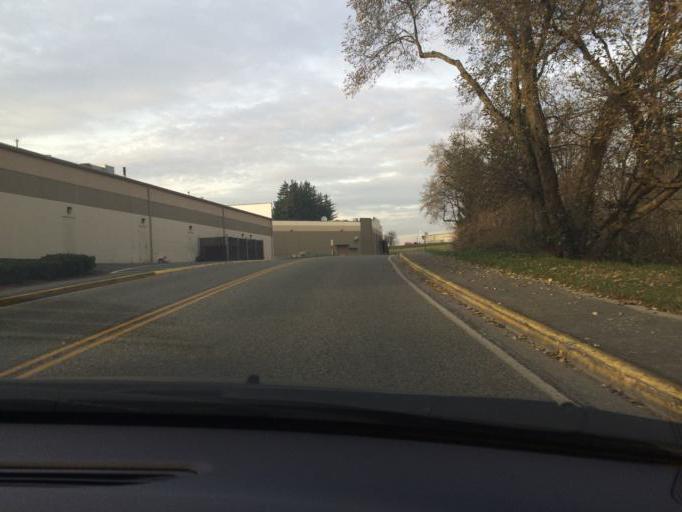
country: US
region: Washington
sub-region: Whatcom County
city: Lynden
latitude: 48.9355
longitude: -122.4817
